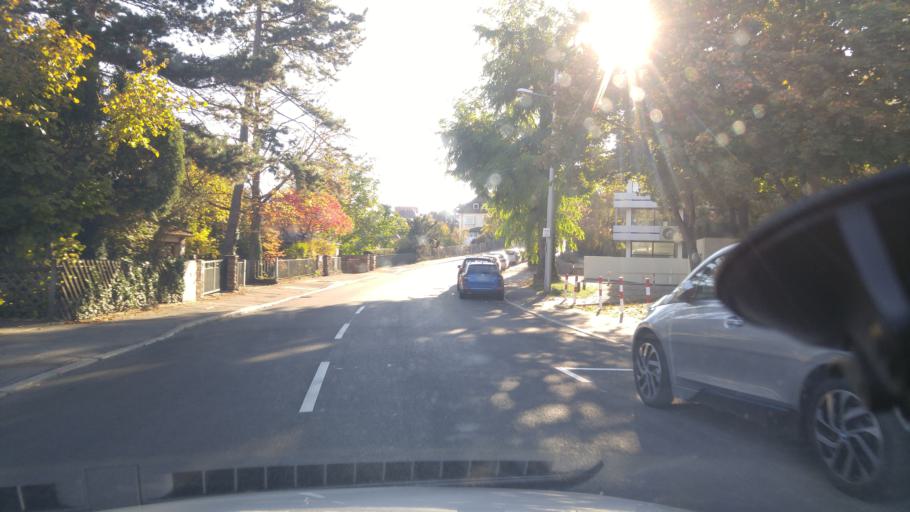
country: DE
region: Baden-Wuerttemberg
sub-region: Regierungsbezirk Stuttgart
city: Stuttgart
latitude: 48.7936
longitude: 9.1741
